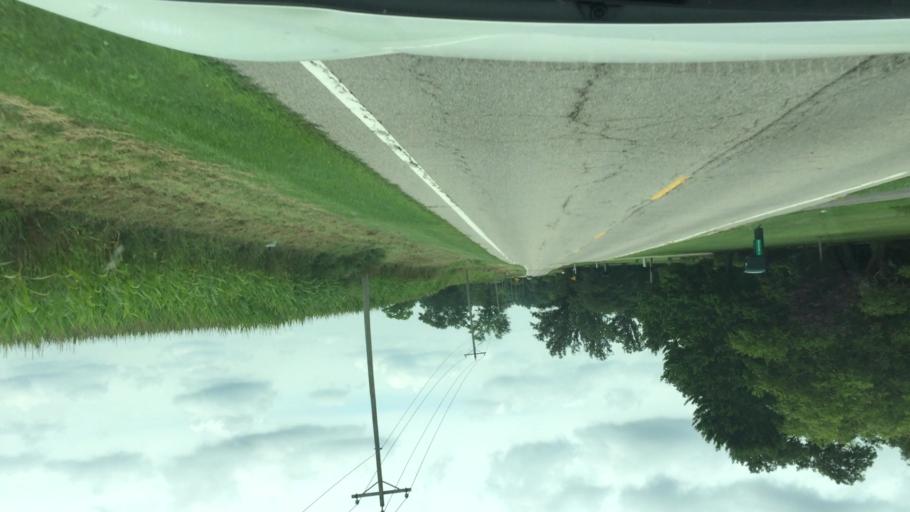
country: US
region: Ohio
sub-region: Champaign County
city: North Lewisburg
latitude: 40.2354
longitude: -83.4681
